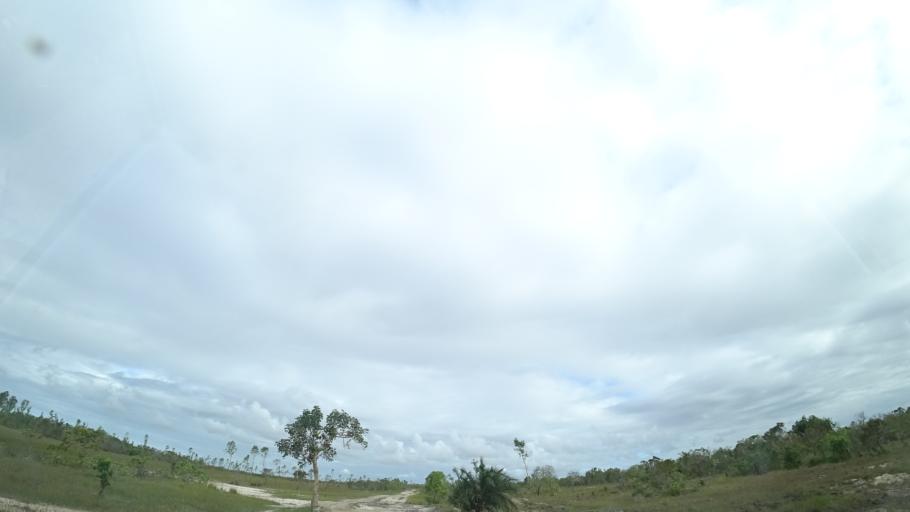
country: MZ
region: Sofala
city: Dondo
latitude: -19.5951
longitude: 35.0847
